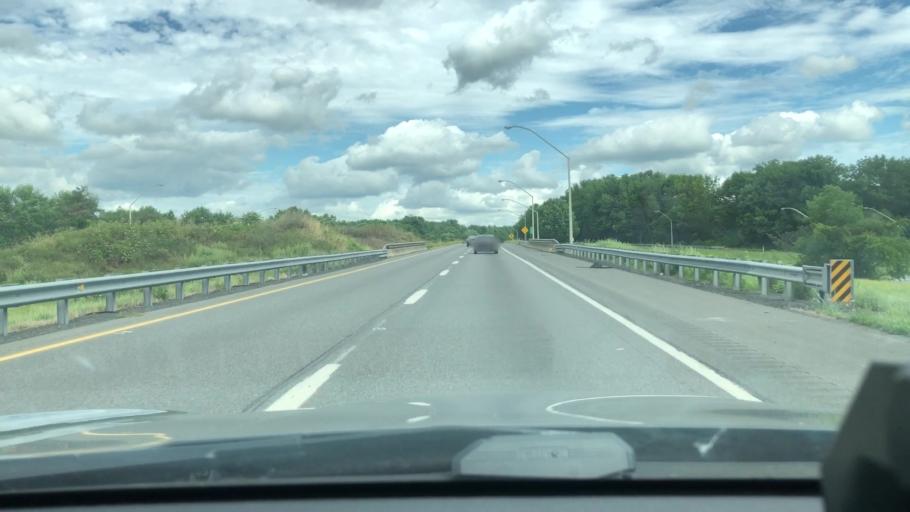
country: US
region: Pennsylvania
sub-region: Northampton County
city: Belfast
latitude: 40.7780
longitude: -75.2822
